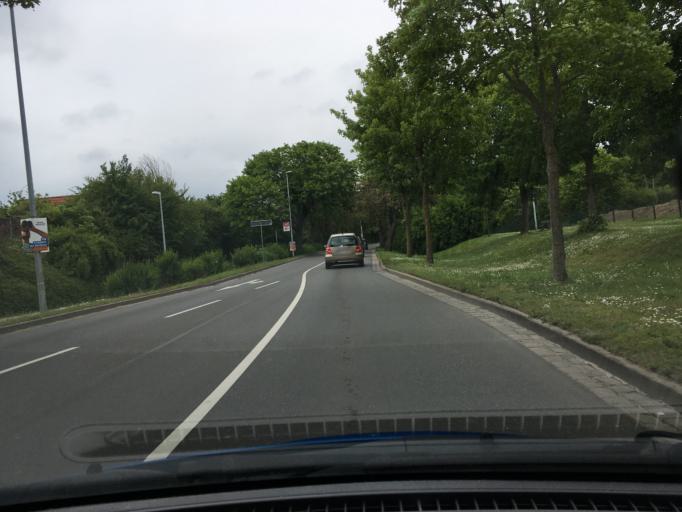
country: DE
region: Mecklenburg-Vorpommern
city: Wismar
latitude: 53.8850
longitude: 11.4333
